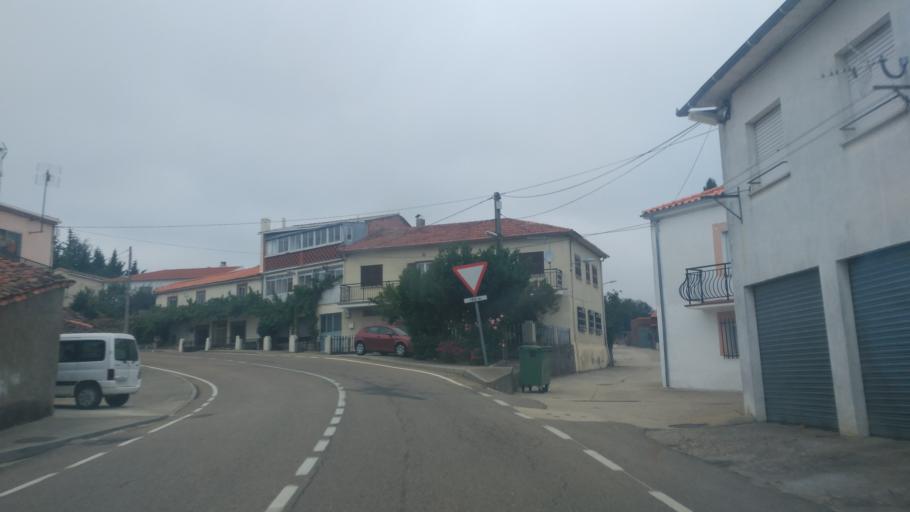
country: ES
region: Castille and Leon
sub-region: Provincia de Salamanca
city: Nava de Francia
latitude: 40.5657
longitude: -6.1266
